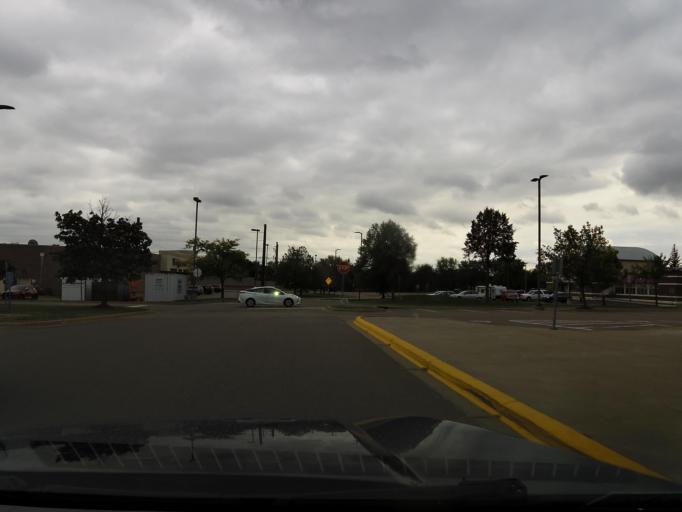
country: US
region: Minnesota
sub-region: Scott County
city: Prior Lake
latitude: 44.7477
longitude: -93.3823
